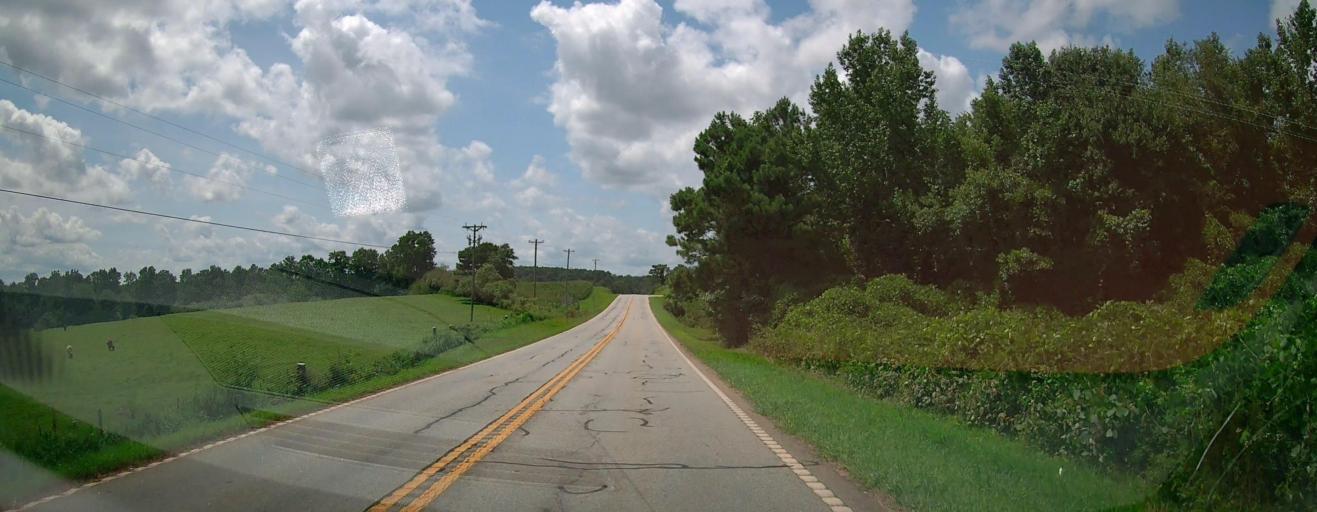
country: US
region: Georgia
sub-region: Carroll County
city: Bowdon
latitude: 33.4137
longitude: -85.2577
